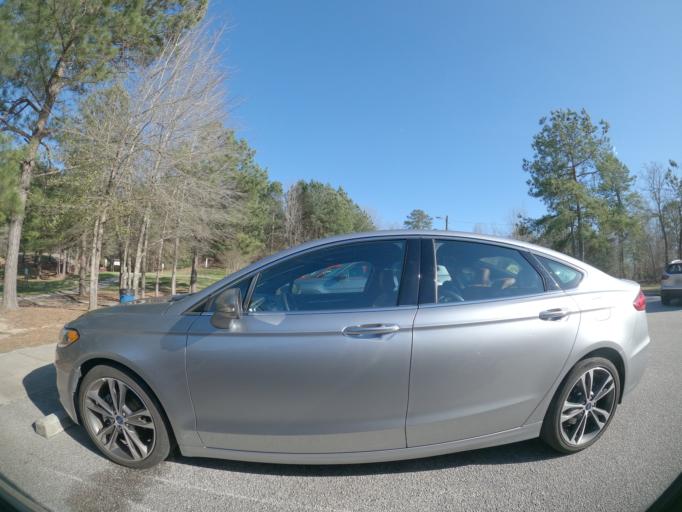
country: US
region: Georgia
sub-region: Columbia County
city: Grovetown
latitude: 33.4565
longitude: -82.2313
